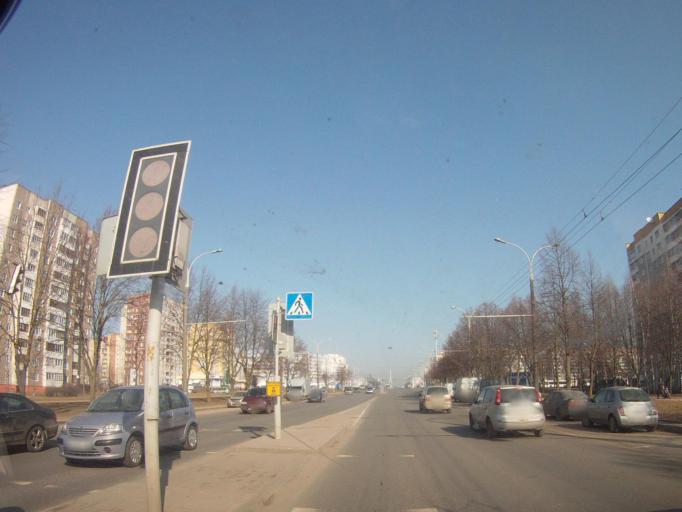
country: BY
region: Minsk
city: Novoye Medvezhino
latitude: 53.8985
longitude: 27.4349
